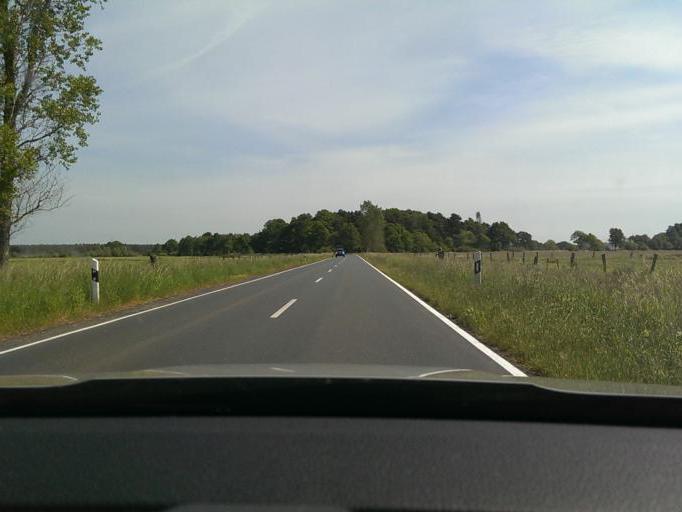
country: DE
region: Lower Saxony
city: Wietze
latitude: 52.6653
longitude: 9.7700
